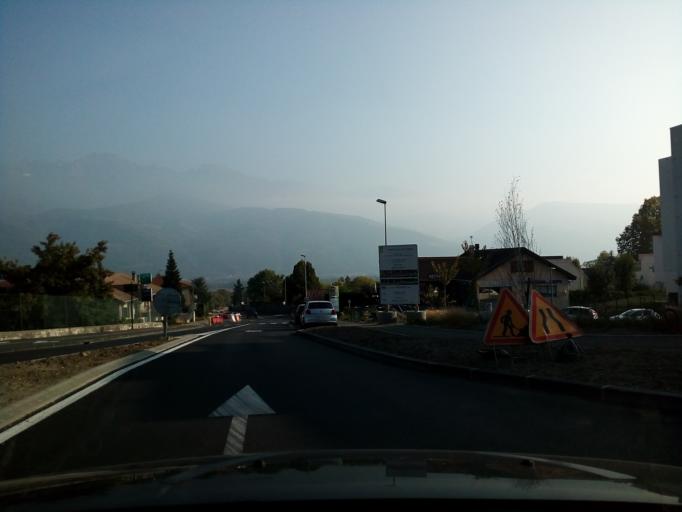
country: FR
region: Rhone-Alpes
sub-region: Departement de l'Isere
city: Saint-Ismier
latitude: 45.2439
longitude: 5.8276
